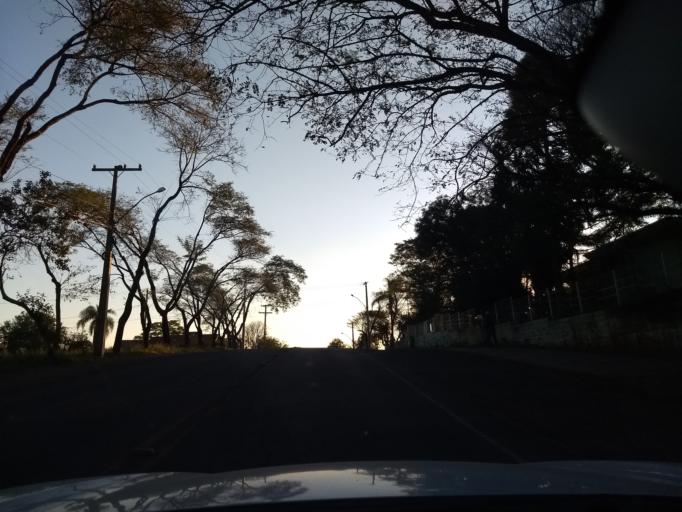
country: BR
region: Rio Grande do Sul
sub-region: Santa Cruz Do Sul
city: Santa Cruz do Sul
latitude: -29.7153
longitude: -52.5097
